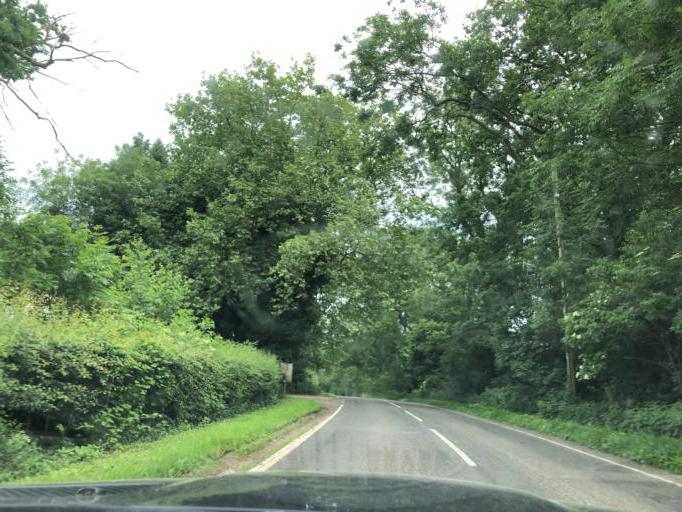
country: GB
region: England
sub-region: Warwickshire
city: Kenilworth
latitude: 52.3272
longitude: -1.6097
